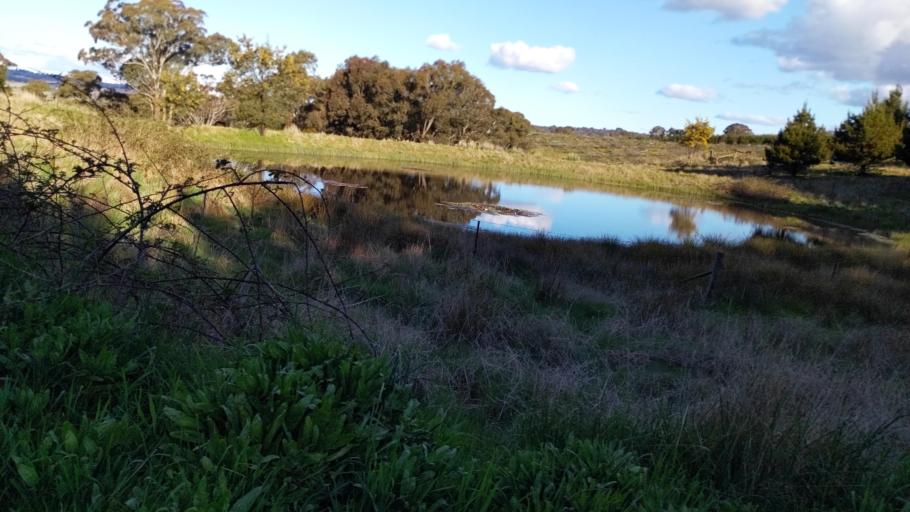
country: AU
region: New South Wales
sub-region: Blayney
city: Millthorpe
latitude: -33.4023
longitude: 149.3121
